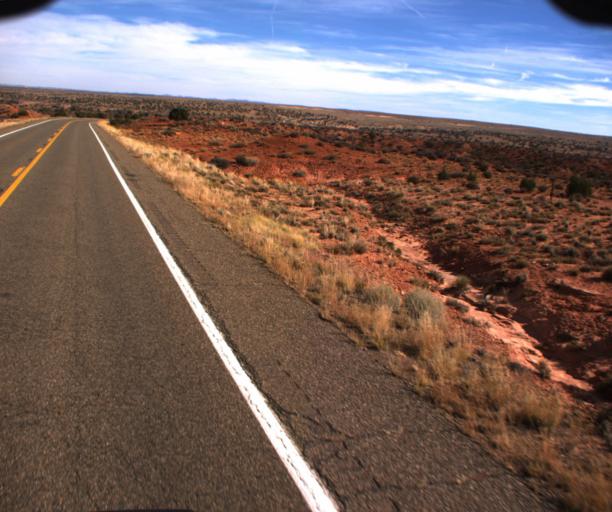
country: US
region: Arizona
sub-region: Coconino County
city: Kaibito
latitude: 36.6027
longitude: -111.0892
